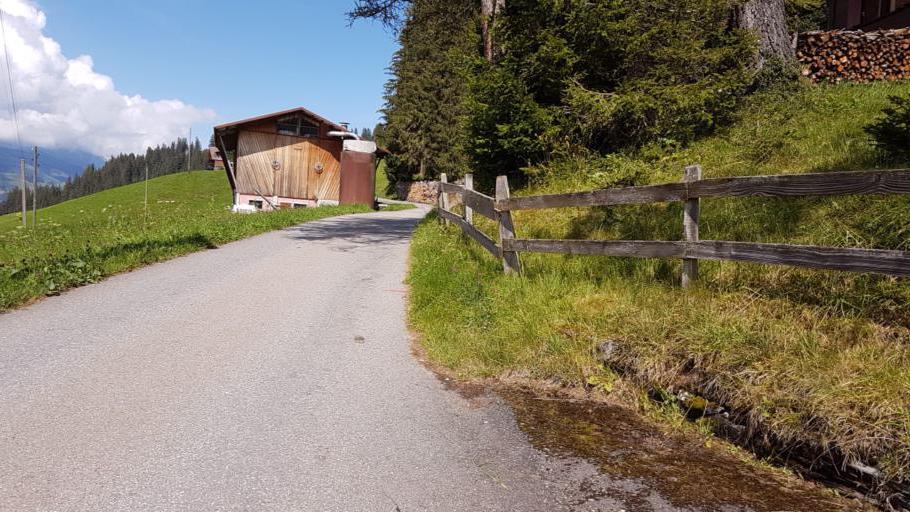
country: CH
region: Bern
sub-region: Frutigen-Niedersimmental District
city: Adelboden
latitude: 46.5073
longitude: 7.5924
